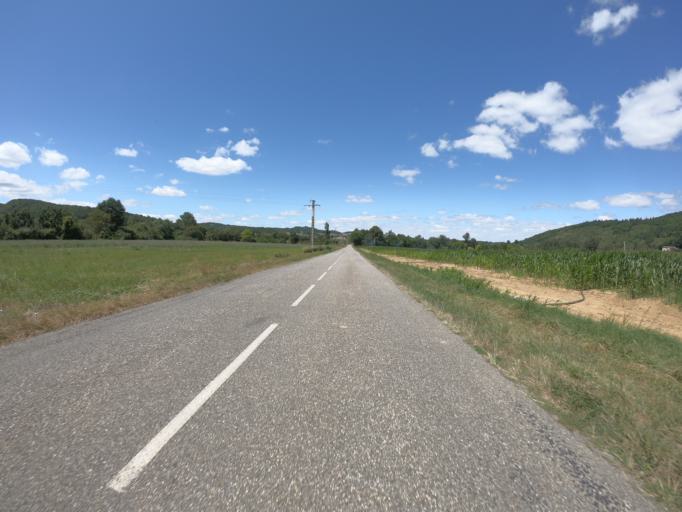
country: FR
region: Midi-Pyrenees
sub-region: Departement de l'Ariege
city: Verniolle
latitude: 43.0528
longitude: 1.7542
